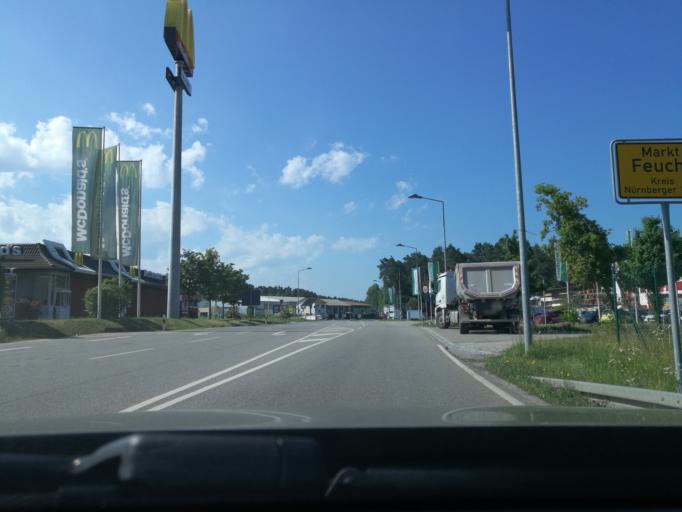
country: DE
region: Bavaria
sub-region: Regierungsbezirk Mittelfranken
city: Feucht
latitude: 49.3657
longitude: 11.2066
